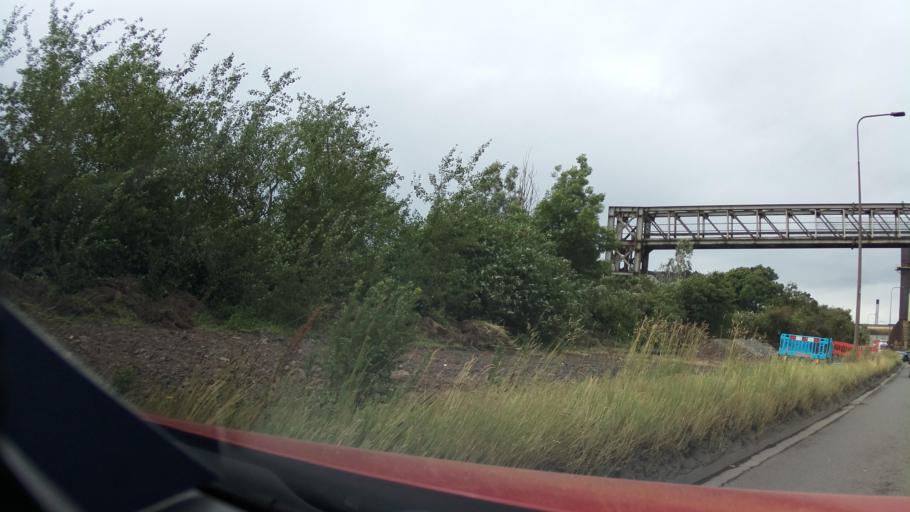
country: GB
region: Wales
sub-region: Cardiff
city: Cardiff
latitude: 51.4808
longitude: -3.1337
